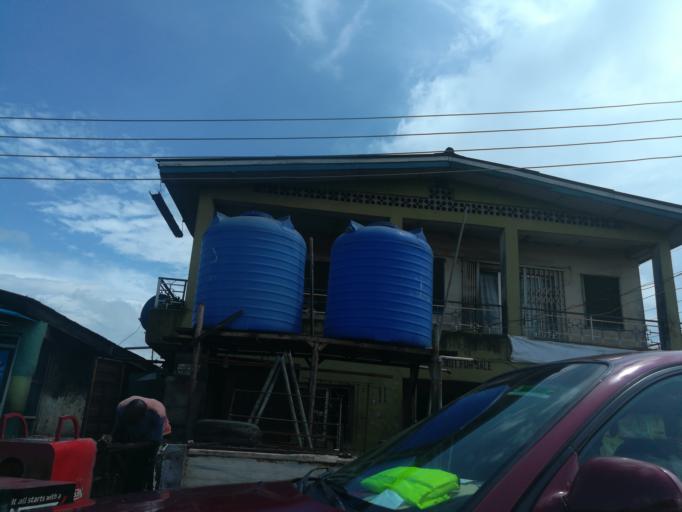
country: NG
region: Lagos
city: Agege
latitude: 6.6227
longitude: 3.3296
